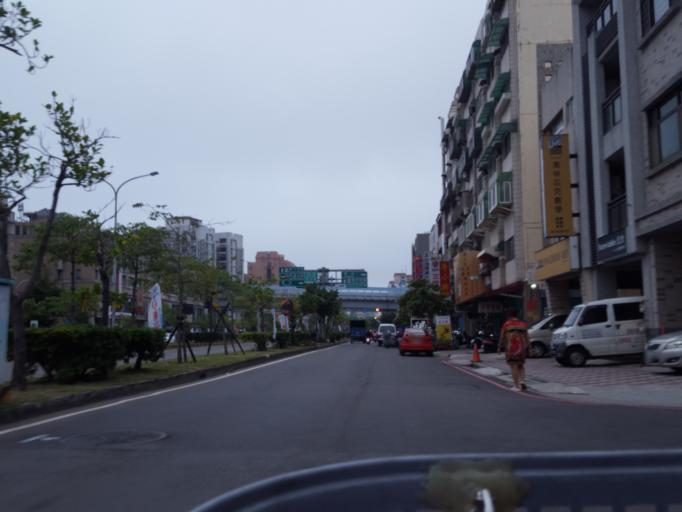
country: TW
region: Taiwan
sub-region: Hsinchu
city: Hsinchu
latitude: 24.8183
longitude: 120.9629
